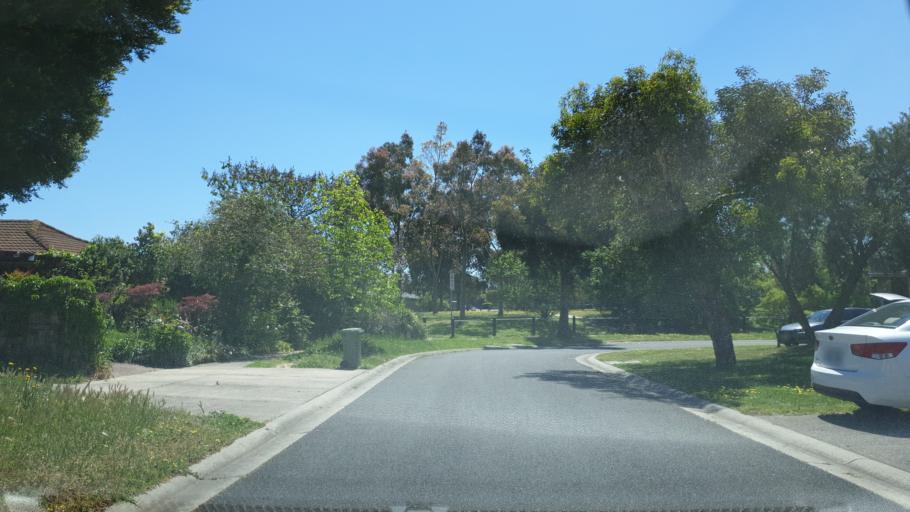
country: AU
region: Victoria
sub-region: Casey
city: Cranbourne North
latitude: -38.0827
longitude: 145.2881
